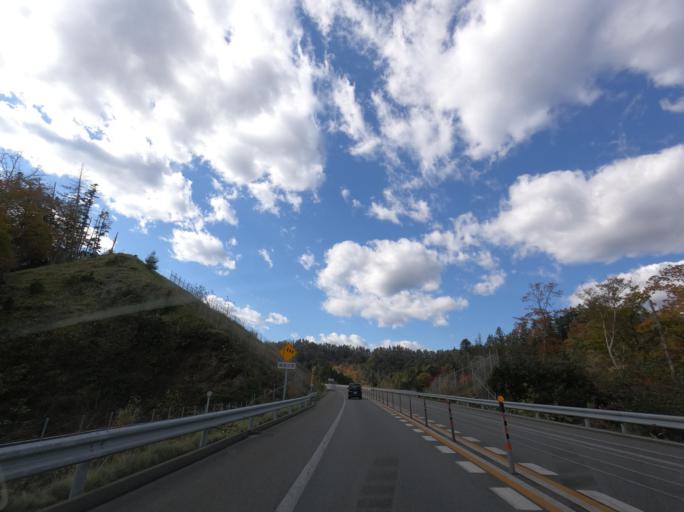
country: JP
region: Hokkaido
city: Kushiro
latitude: 43.0799
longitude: 144.0493
